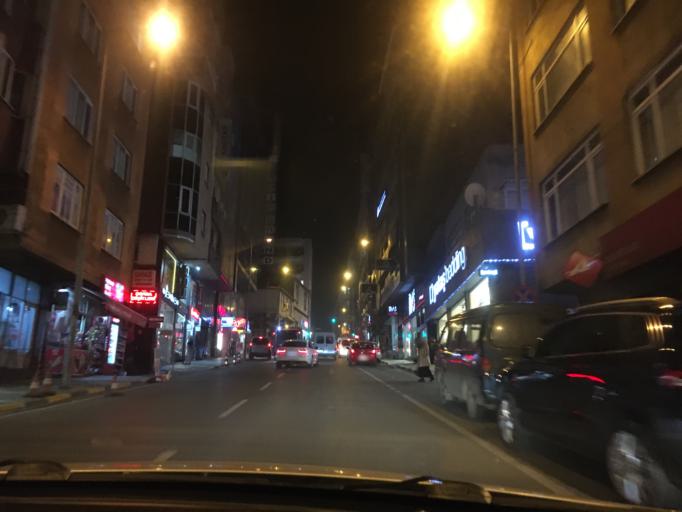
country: TR
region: Trabzon
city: Trabzon
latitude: 41.0074
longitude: 39.7258
